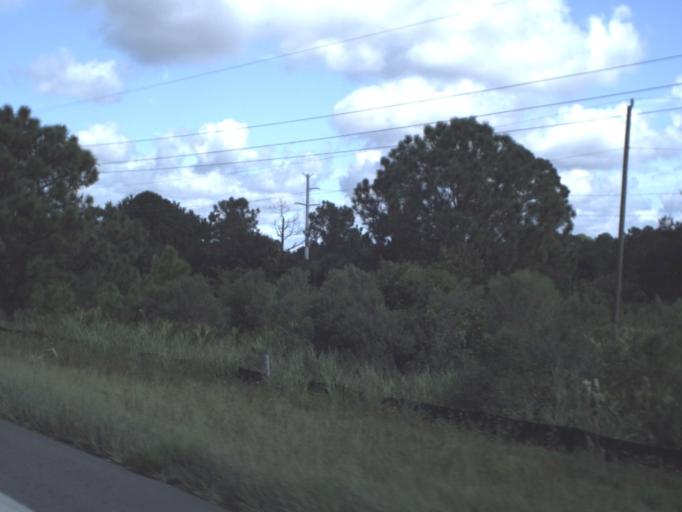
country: US
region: Florida
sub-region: Charlotte County
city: Port Charlotte
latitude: 27.0363
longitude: -82.0584
